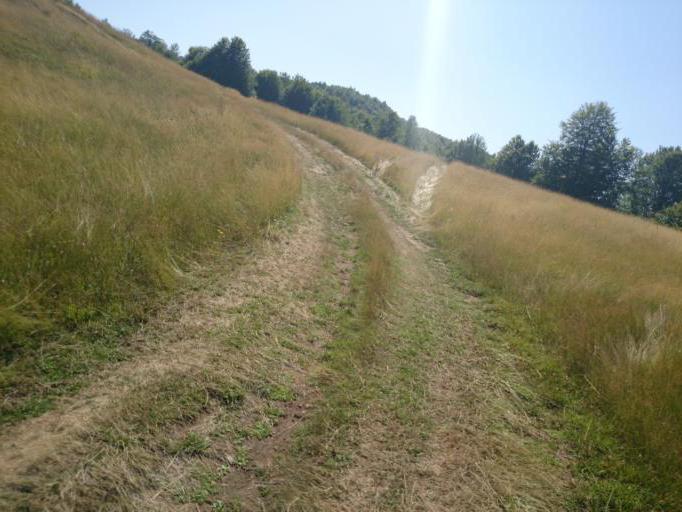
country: AL
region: Elbasan
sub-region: Rrethi i Librazhdit
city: Orenje
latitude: 41.3337
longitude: 20.1738
